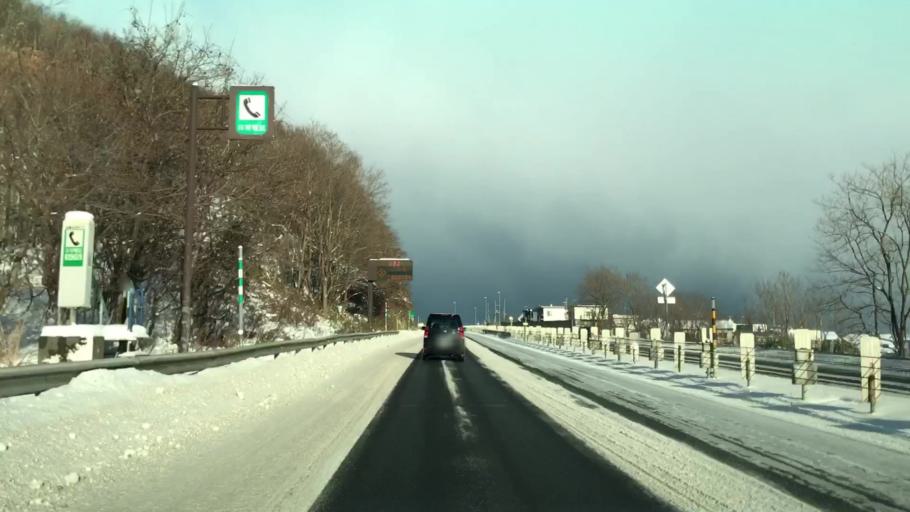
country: JP
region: Hokkaido
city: Sapporo
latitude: 43.1061
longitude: 141.2426
